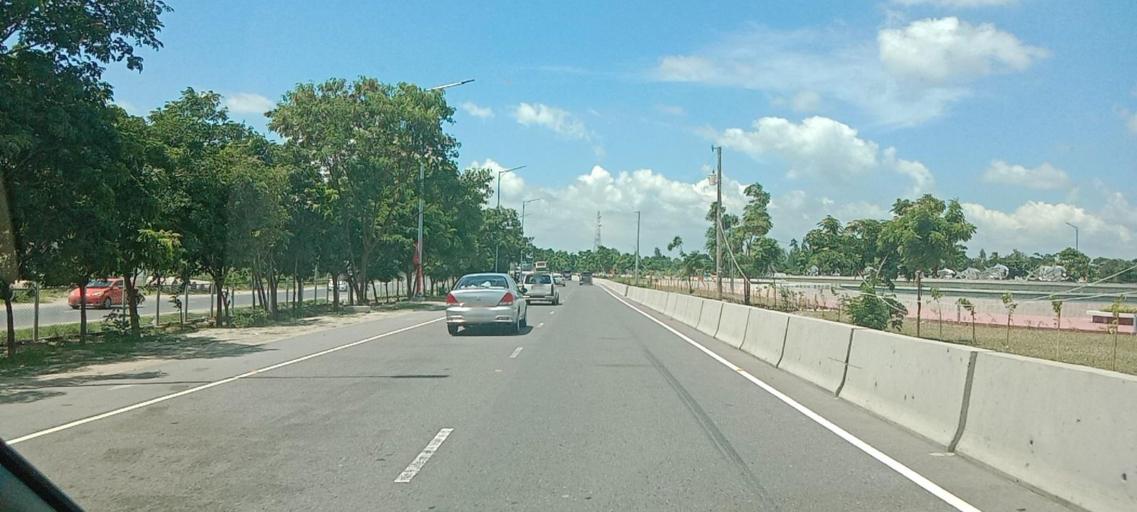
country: BD
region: Dhaka
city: Dohar
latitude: 23.4789
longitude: 90.2665
